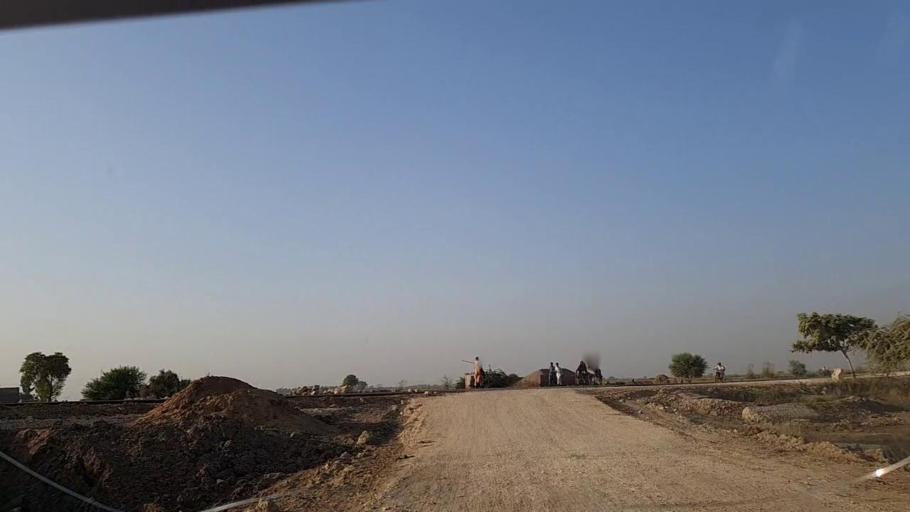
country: PK
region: Sindh
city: Rustam jo Goth
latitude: 27.9752
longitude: 68.8052
